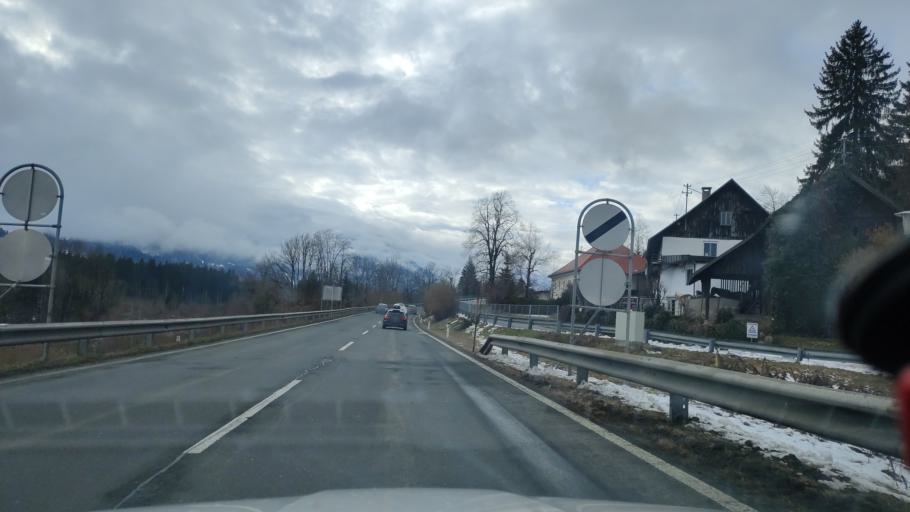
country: AT
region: Carinthia
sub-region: Politischer Bezirk Hermagor
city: Hermagor
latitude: 46.6217
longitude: 13.3094
